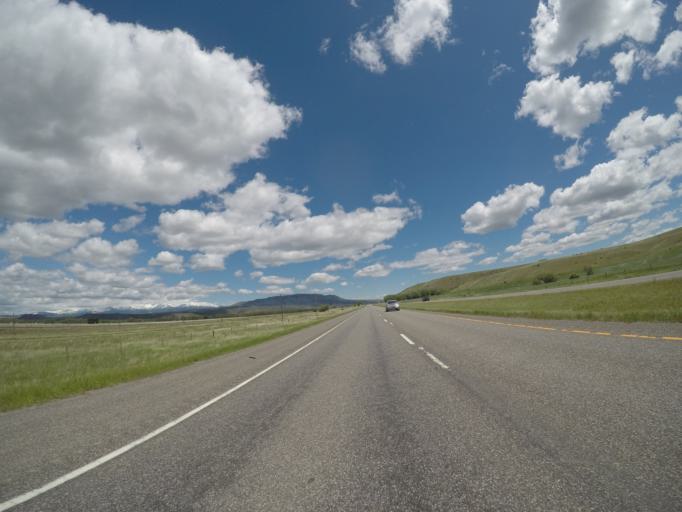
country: US
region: Montana
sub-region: Park County
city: Livingston
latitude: 45.7003
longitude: -110.4716
